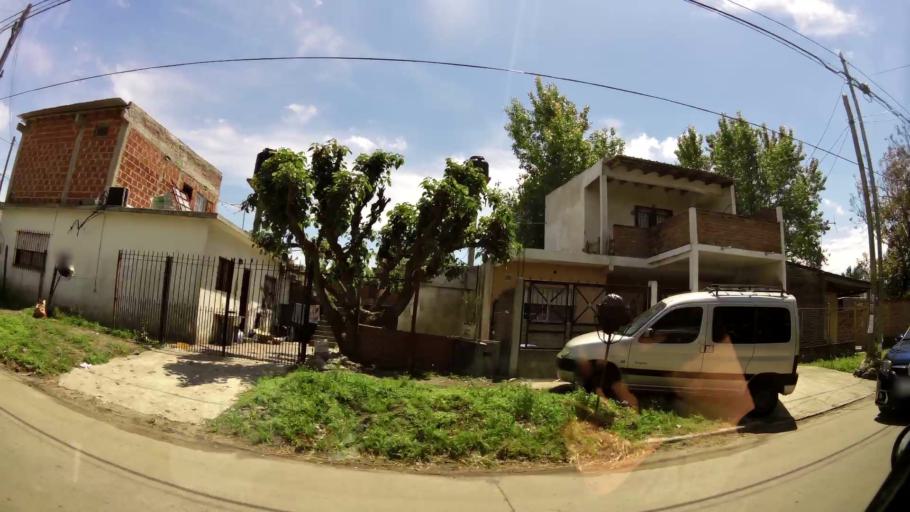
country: AR
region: Buenos Aires
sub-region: Partido de Quilmes
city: Quilmes
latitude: -34.7925
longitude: -58.2722
